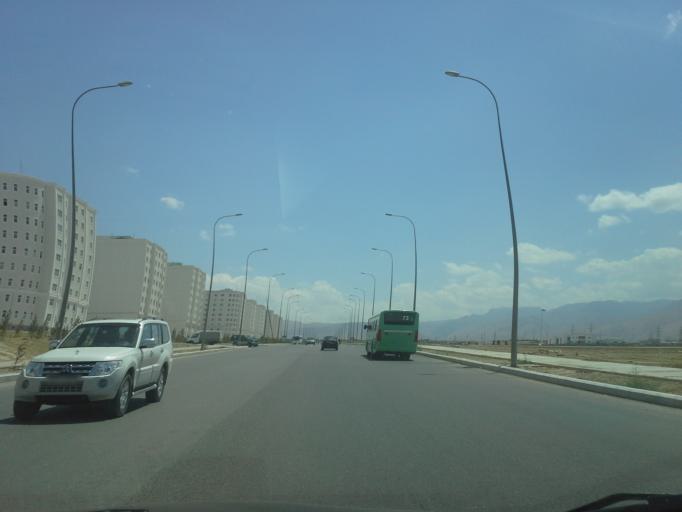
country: TM
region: Ahal
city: Ashgabat
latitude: 37.8938
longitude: 58.4056
